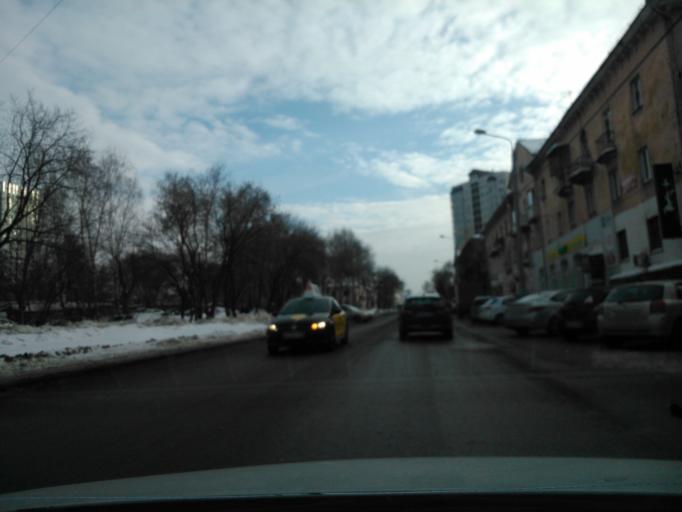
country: RU
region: Perm
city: Perm
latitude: 58.0012
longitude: 56.2395
